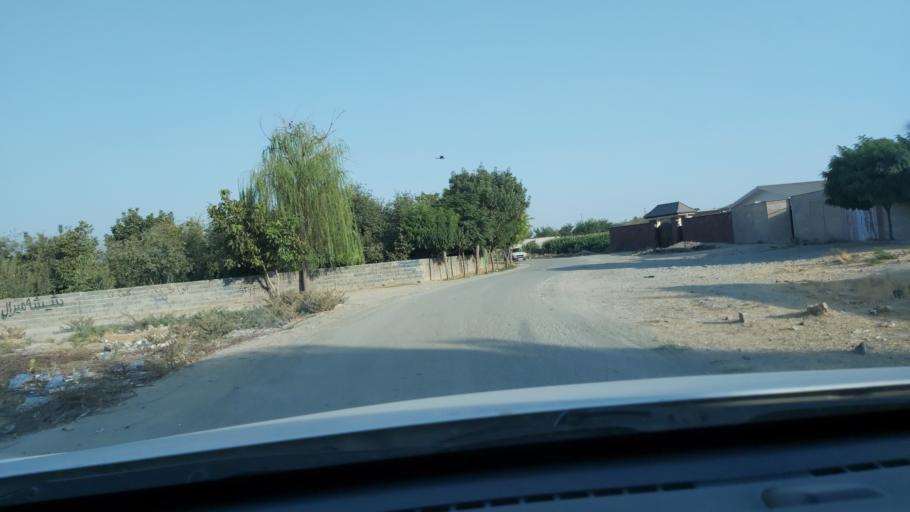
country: IR
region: Alborz
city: Hashtgerd
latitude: 35.8595
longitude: 50.6940
